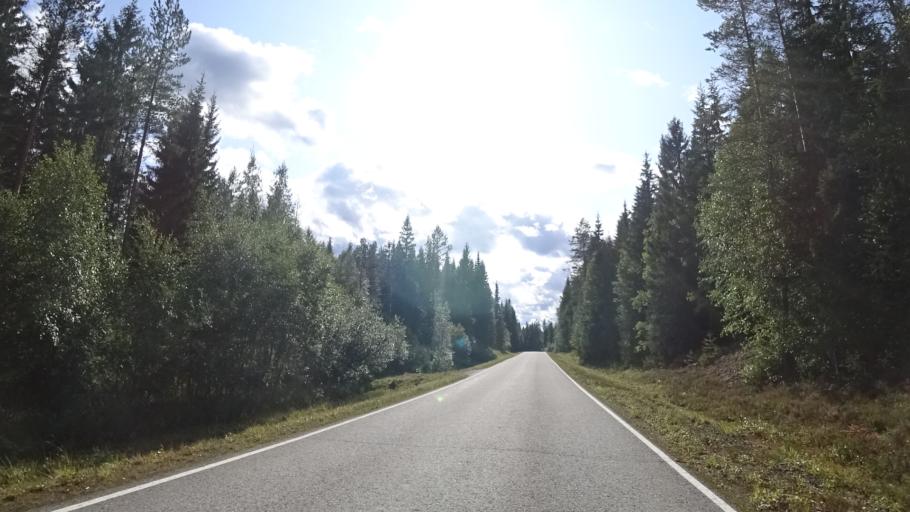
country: RU
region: Republic of Karelia
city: Vyartsilya
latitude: 62.2445
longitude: 30.7126
